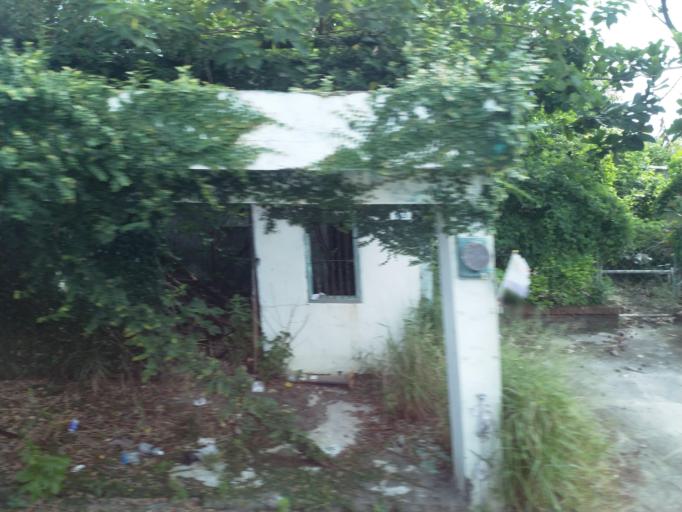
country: TW
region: Taiwan
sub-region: Pingtung
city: Pingtung
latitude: 22.8798
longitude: 120.4963
